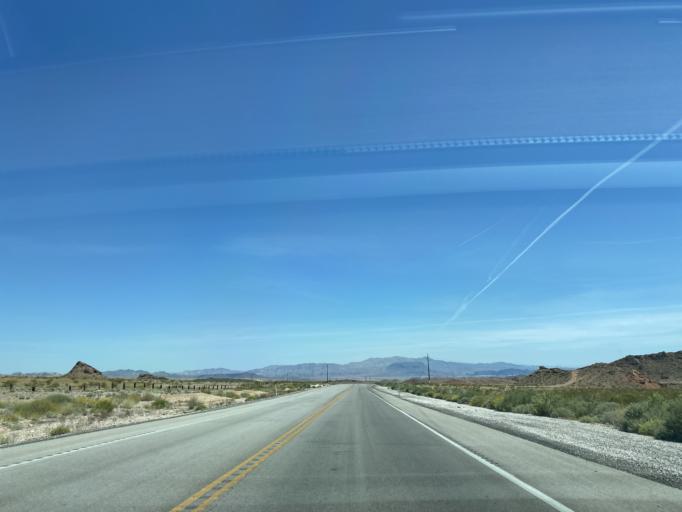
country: US
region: Nevada
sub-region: Clark County
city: Nellis Air Force Base
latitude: 36.2056
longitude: -114.9460
